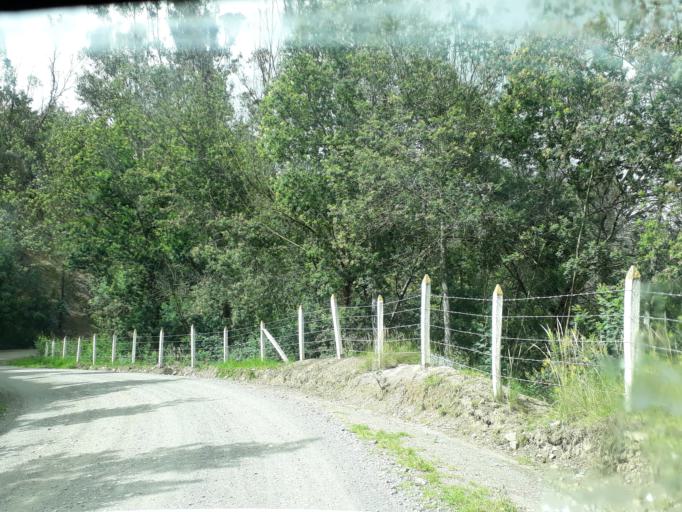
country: CO
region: Cundinamarca
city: La Mesa
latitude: 5.3004
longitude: -73.9048
